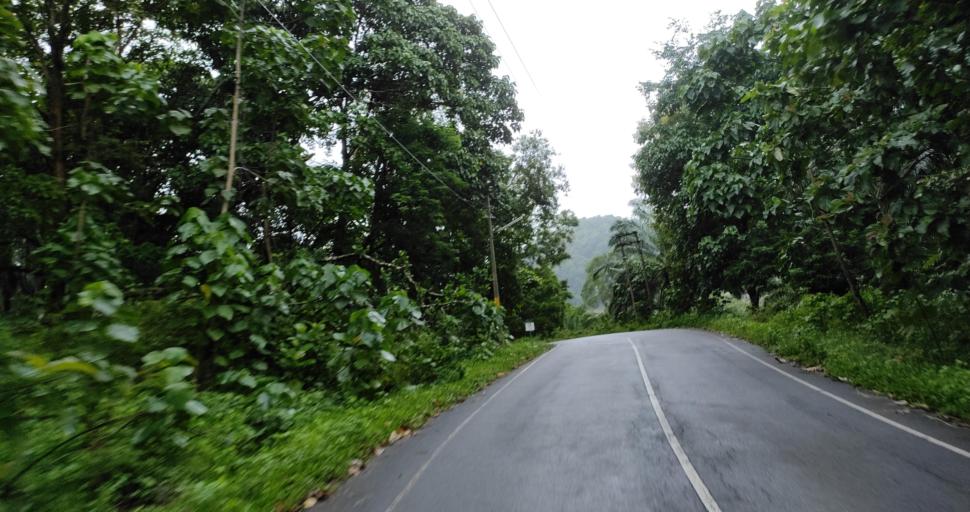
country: IN
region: Kerala
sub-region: Ernakulam
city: Angamali
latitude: 10.2887
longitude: 76.5504
